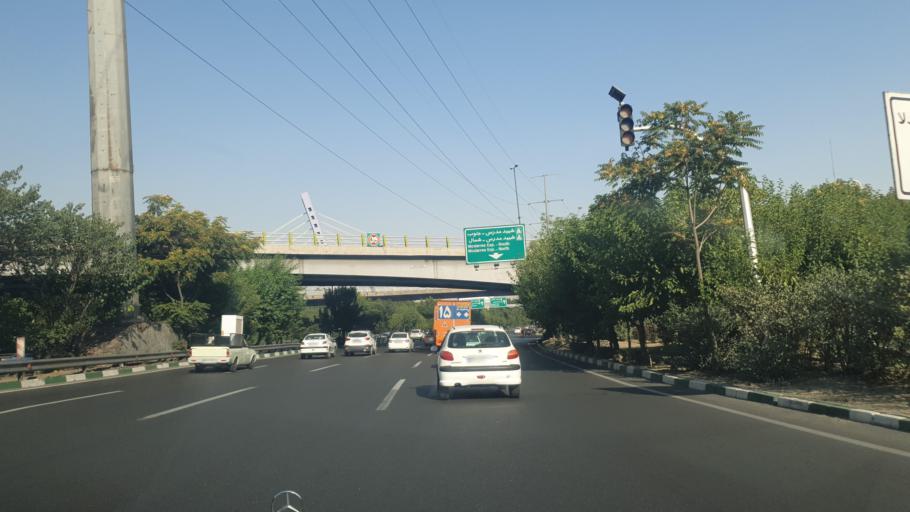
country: IR
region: Tehran
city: Tajrish
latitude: 35.7518
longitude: 51.4167
